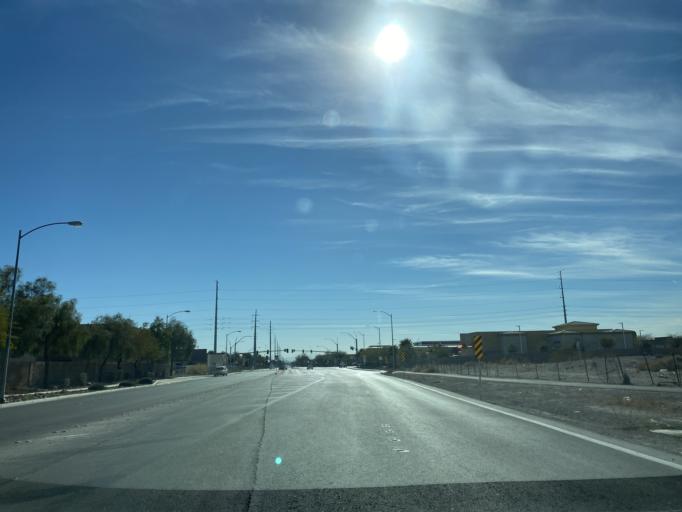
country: US
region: Nevada
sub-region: Clark County
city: North Las Vegas
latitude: 36.2782
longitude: -115.1441
